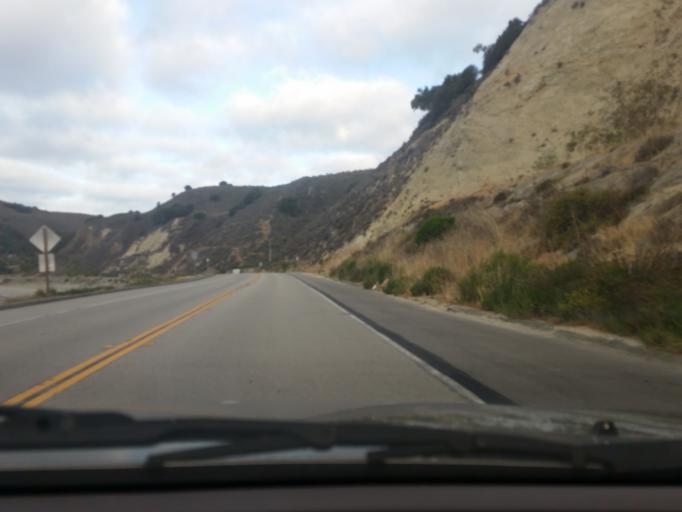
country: US
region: California
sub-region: San Luis Obispo County
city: Avila Beach
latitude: 35.1784
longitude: -120.7440
